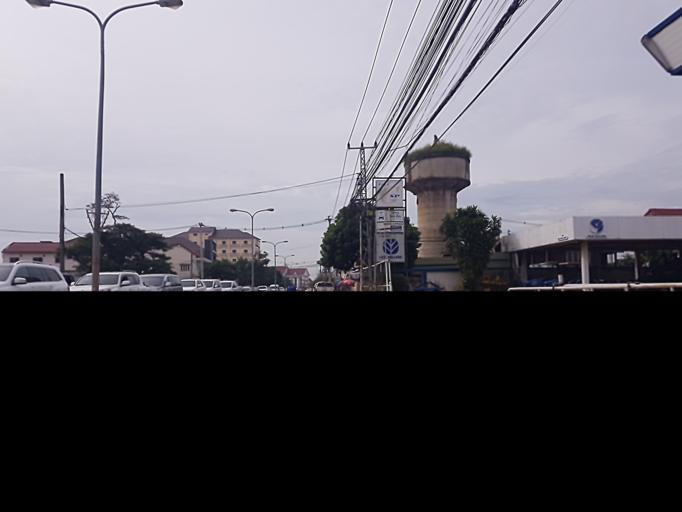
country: LA
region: Vientiane
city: Vientiane
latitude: 17.9504
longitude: 102.6192
